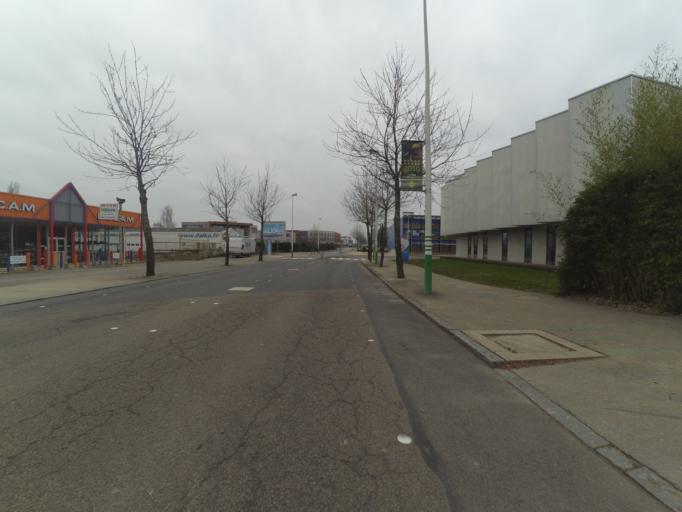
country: FR
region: Pays de la Loire
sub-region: Departement de la Loire-Atlantique
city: Saint-Herblain
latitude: 47.2210
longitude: -1.6402
